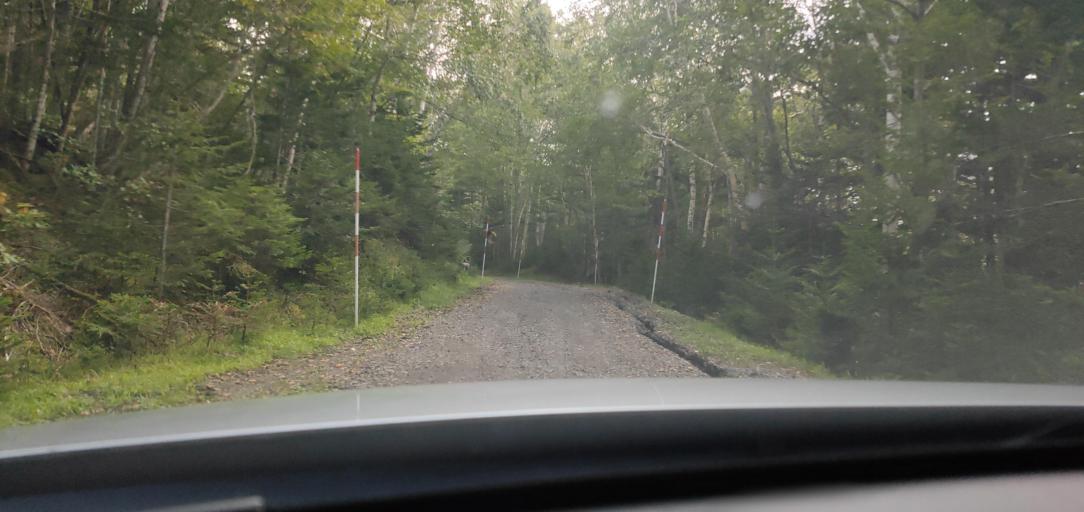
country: JP
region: Hokkaido
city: Kitami
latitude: 43.3733
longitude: 143.9634
